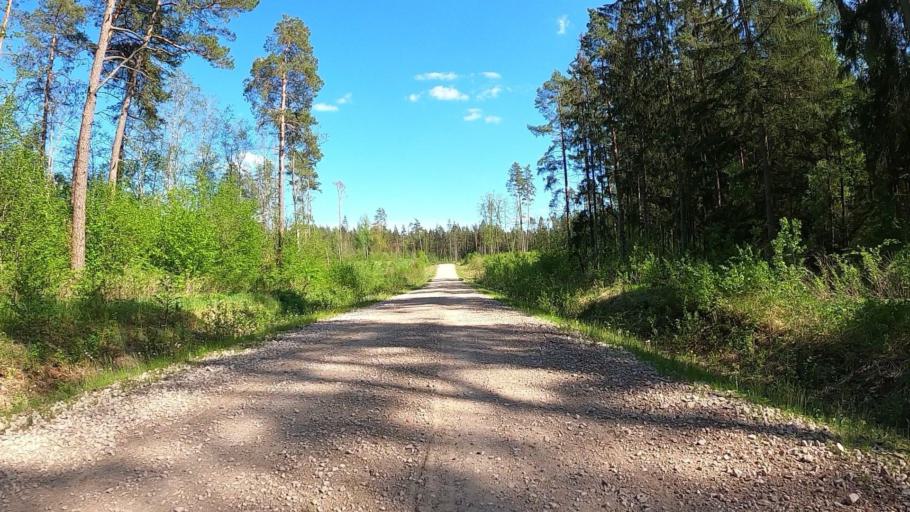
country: LV
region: Baldone
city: Baldone
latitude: 56.7901
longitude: 24.3365
